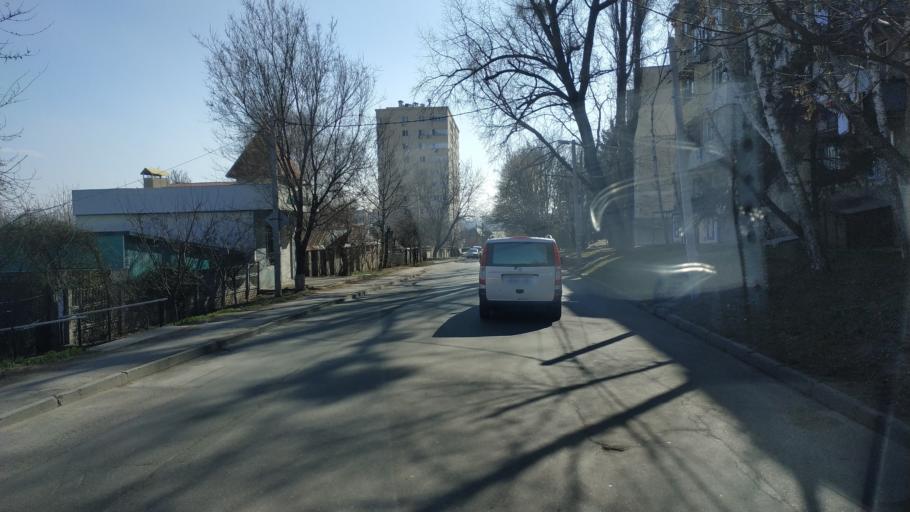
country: MD
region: Chisinau
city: Chisinau
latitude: 47.0316
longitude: 28.8000
